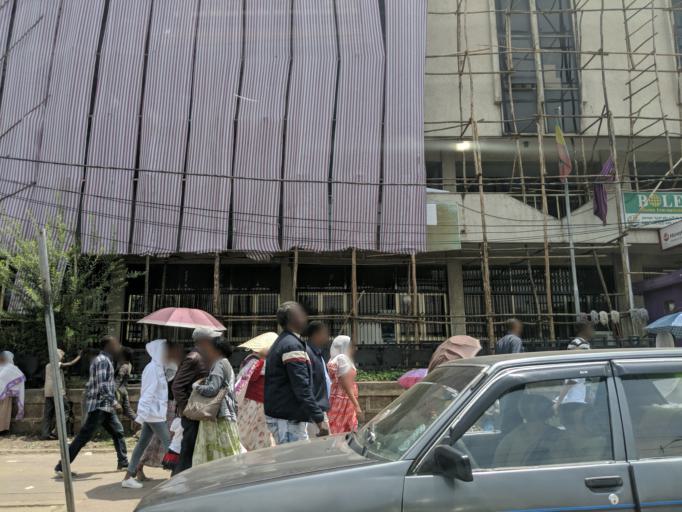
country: ET
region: Adis Abeba
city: Addis Ababa
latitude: 8.9528
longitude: 38.7634
